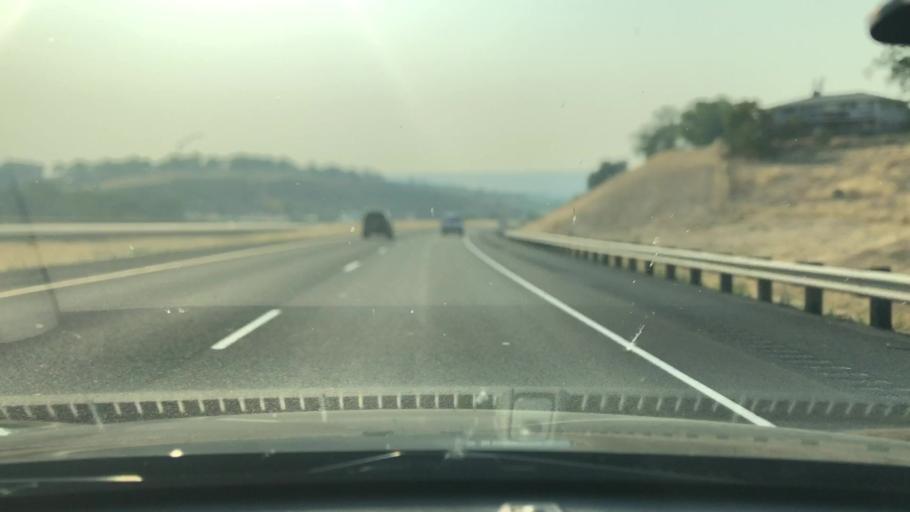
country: US
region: Oregon
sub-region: Umatilla County
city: Pendleton
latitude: 45.6614
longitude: -118.8000
